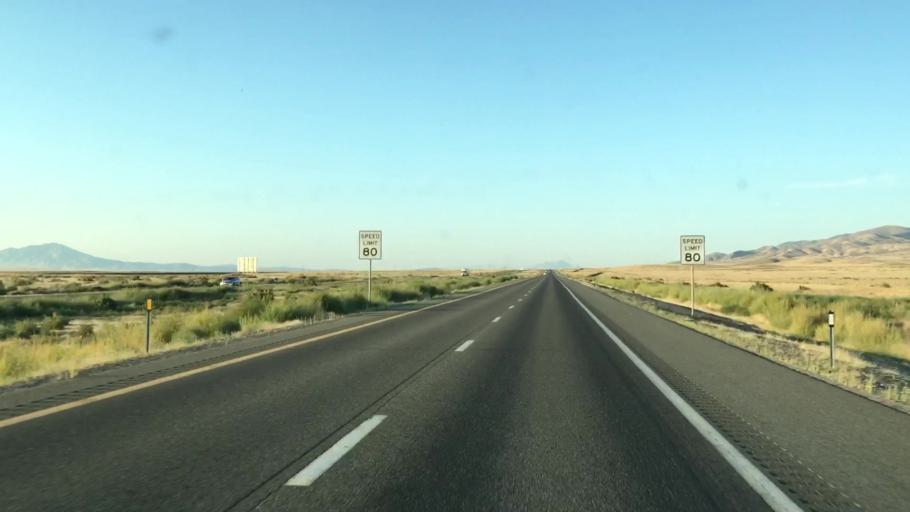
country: US
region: Nevada
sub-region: Humboldt County
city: Winnemucca
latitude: 40.7079
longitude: -118.0463
